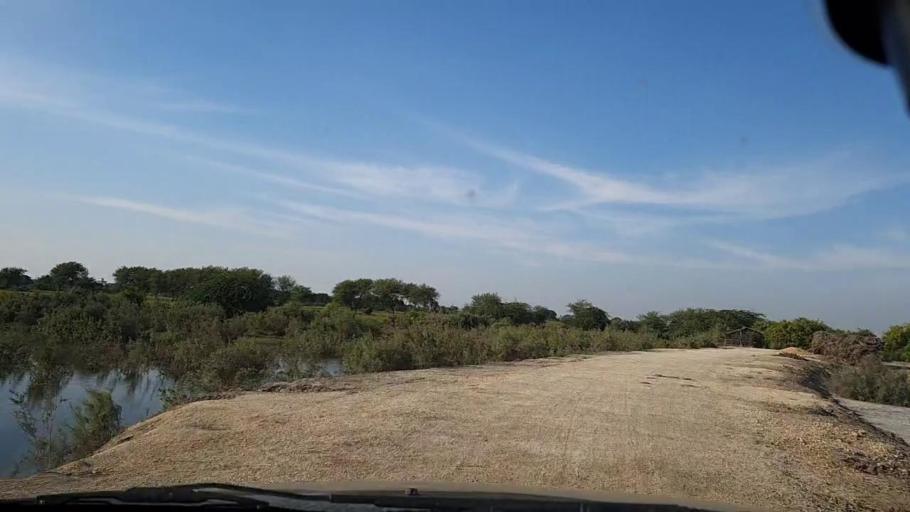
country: PK
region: Sindh
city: Mirpur Batoro
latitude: 24.6365
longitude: 68.2979
